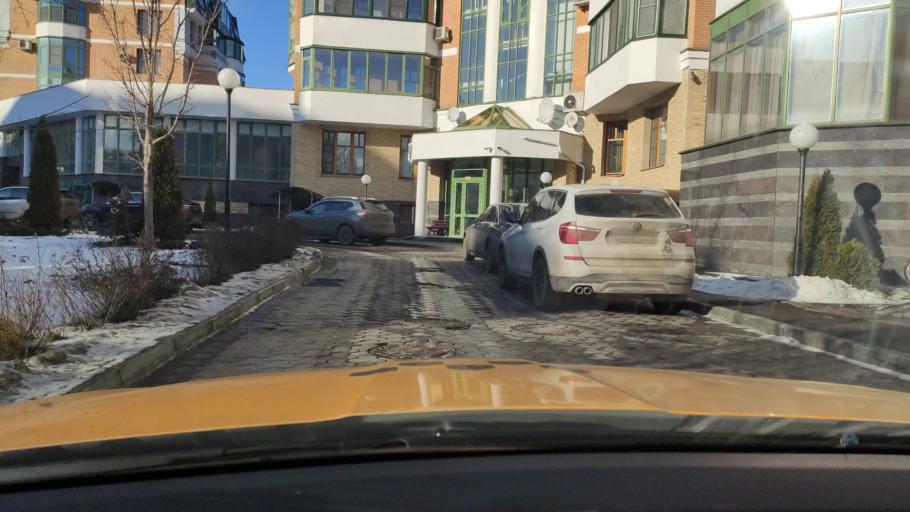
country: RU
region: Moscow
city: Rublevo
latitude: 55.7703
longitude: 37.3981
